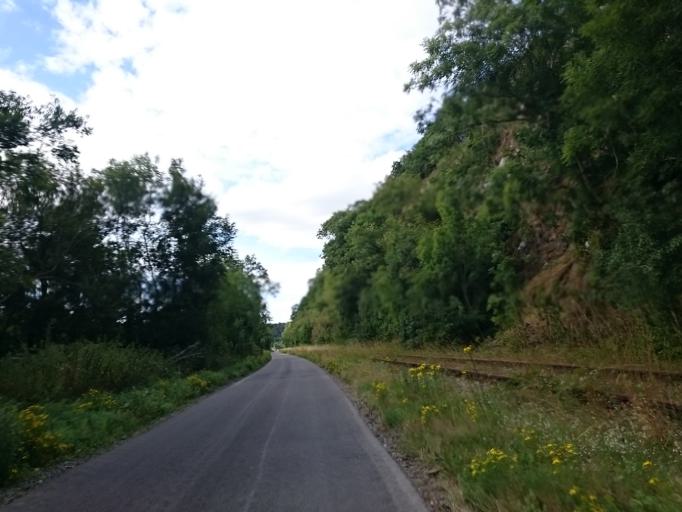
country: FR
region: Lower Normandy
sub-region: Departement du Calvados
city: Thury-Harcourt
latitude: 49.0280
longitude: -0.4643
